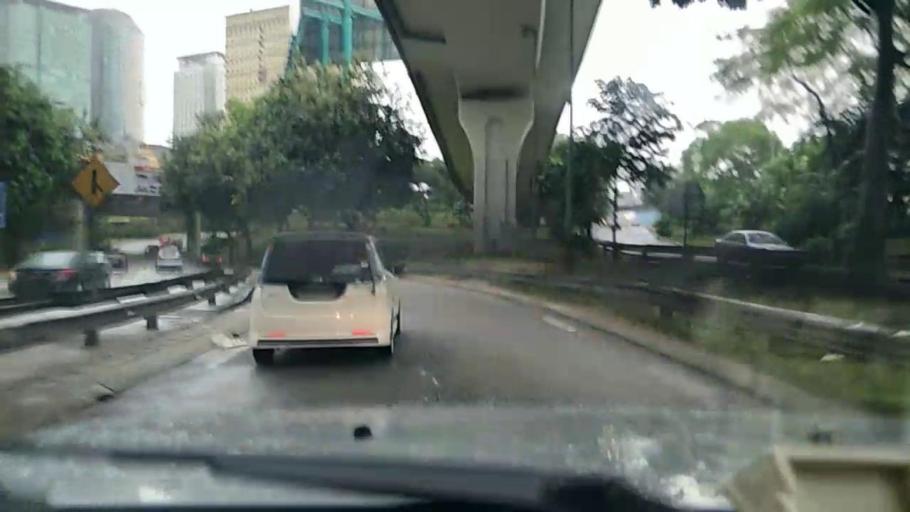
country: MY
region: Kuala Lumpur
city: Kuala Lumpur
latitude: 3.1148
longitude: 101.6789
